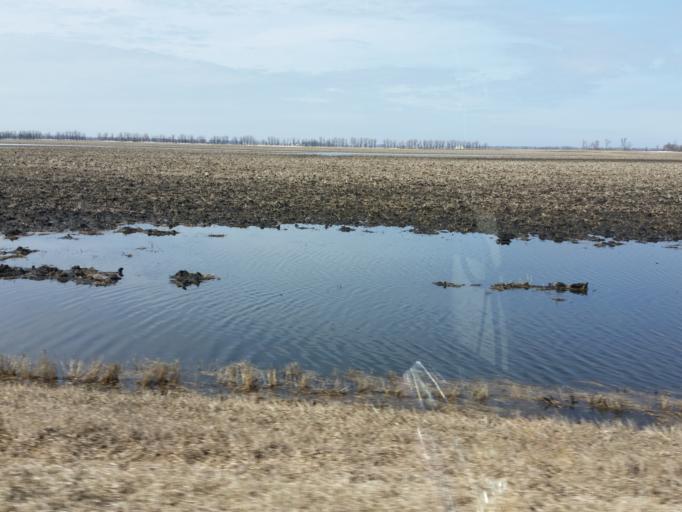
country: US
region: North Dakota
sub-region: Walsh County
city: Grafton
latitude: 48.3378
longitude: -97.2111
